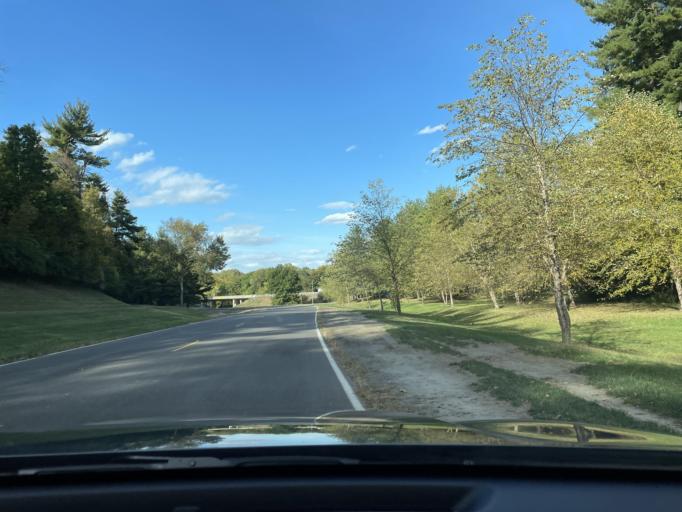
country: US
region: Kansas
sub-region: Doniphan County
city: Elwood
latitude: 39.7251
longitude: -94.8444
